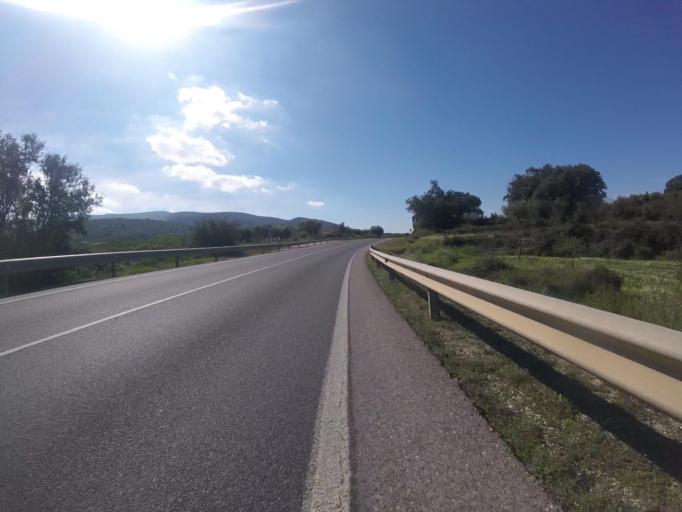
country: ES
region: Valencia
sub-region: Provincia de Castello
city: Sarratella
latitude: 40.3288
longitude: -0.0161
